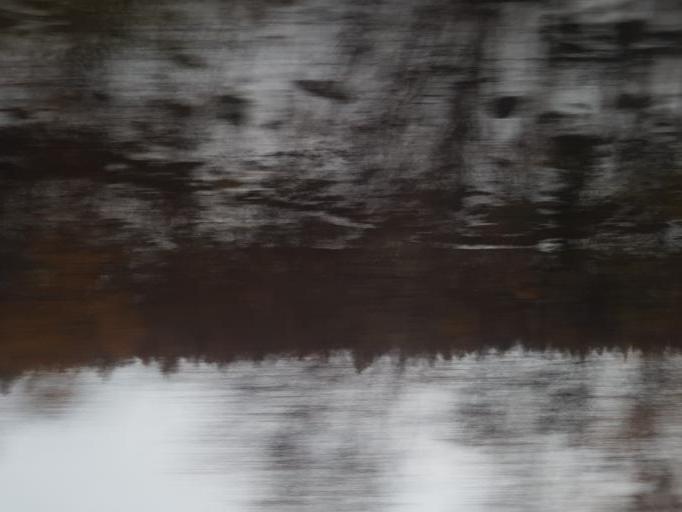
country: NO
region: Oppland
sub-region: Dovre
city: Dovre
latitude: 62.1671
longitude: 9.3866
